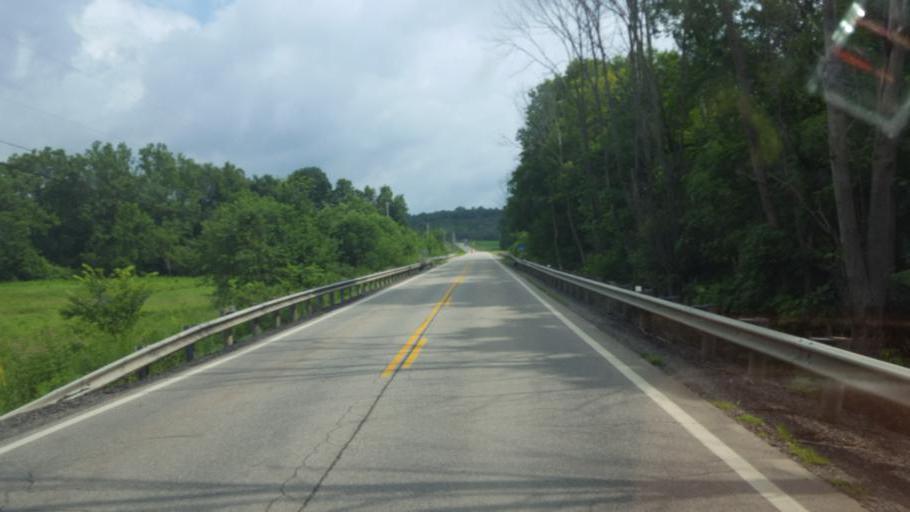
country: US
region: Ohio
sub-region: Columbiana County
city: Lisbon
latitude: 40.7010
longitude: -80.8080
